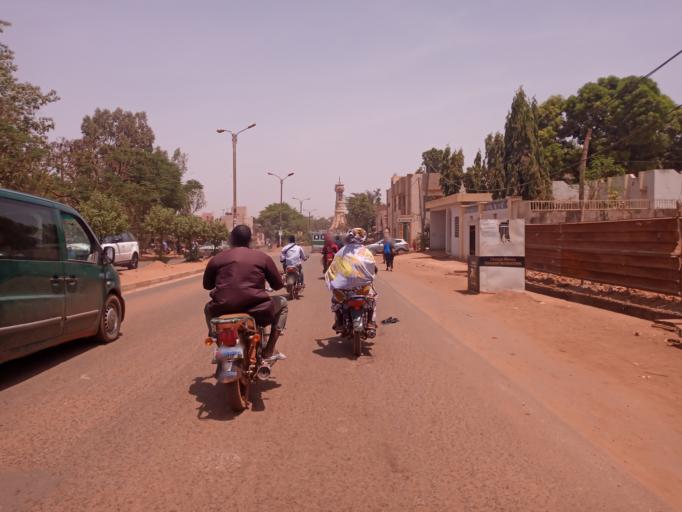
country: ML
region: Bamako
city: Bamako
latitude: 12.5814
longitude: -7.9458
